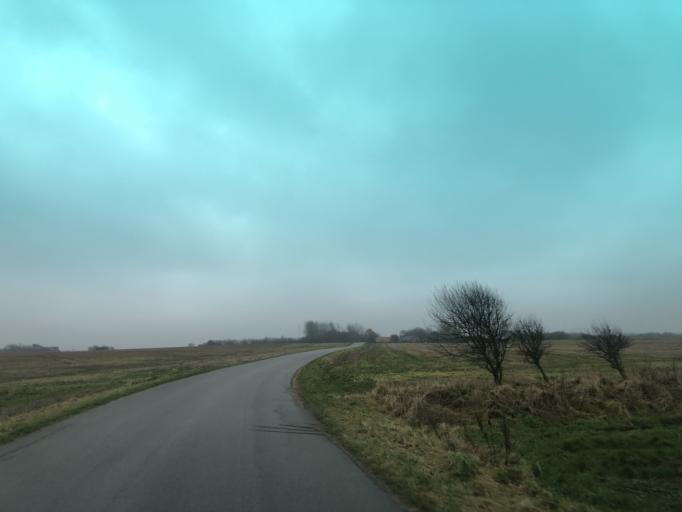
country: DK
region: Central Jutland
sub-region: Struer Kommune
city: Struer
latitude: 56.4414
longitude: 8.5870
